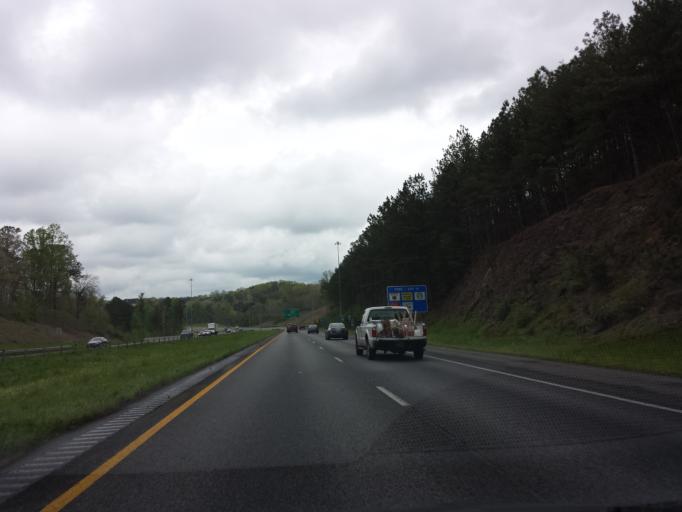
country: US
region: Georgia
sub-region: Cherokee County
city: Canton
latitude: 34.2277
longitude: -84.4720
